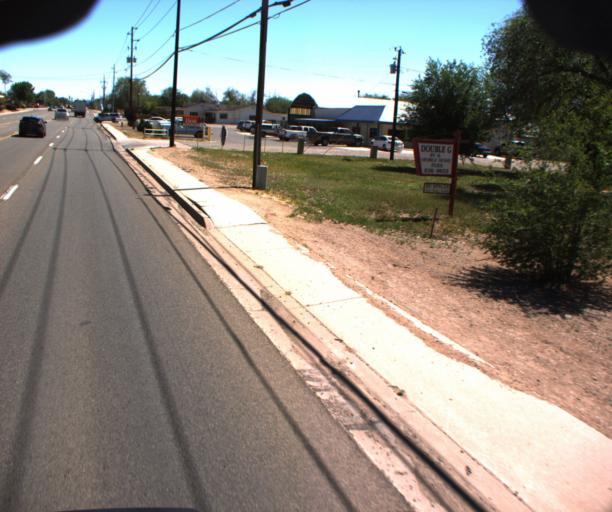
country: US
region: Arizona
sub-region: Yavapai County
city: Chino Valley
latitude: 34.7637
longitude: -112.4536
